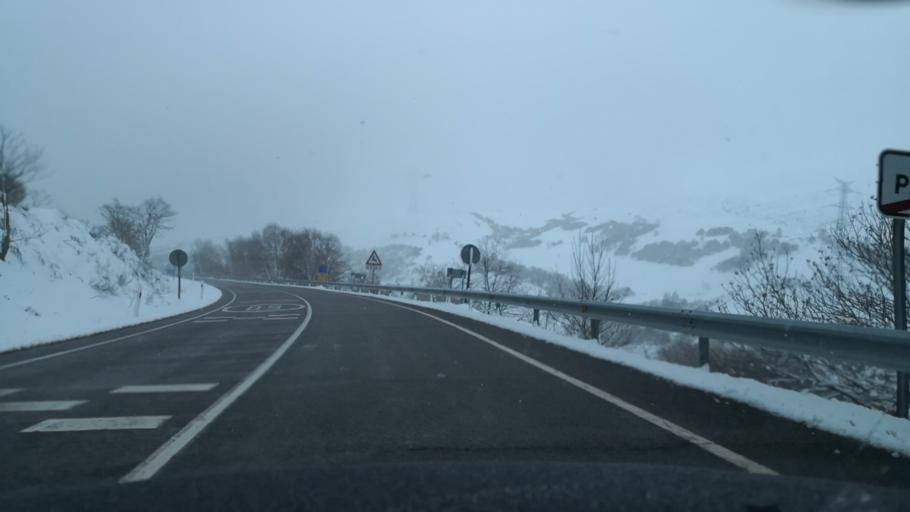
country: ES
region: Castille and Leon
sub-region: Provincia de Zamora
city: Lubian
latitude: 42.0329
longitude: -6.8338
